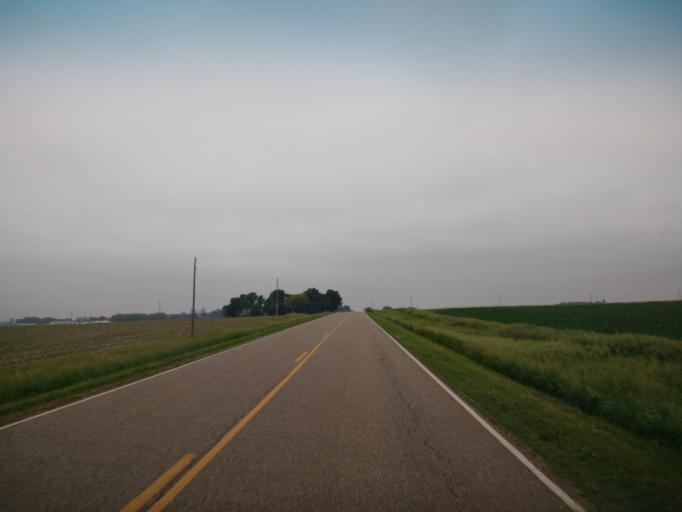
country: US
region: Iowa
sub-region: Sioux County
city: Alton
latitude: 43.0565
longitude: -95.8995
